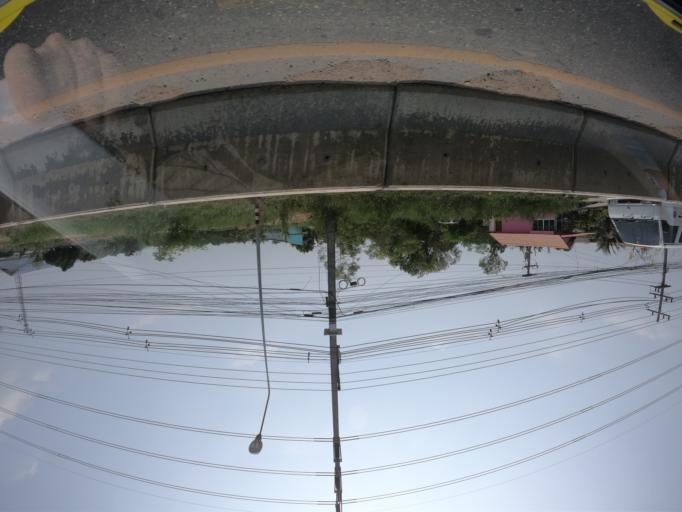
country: TH
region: Pathum Thani
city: Ban Lam Luk Ka
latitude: 13.9464
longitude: 100.7829
